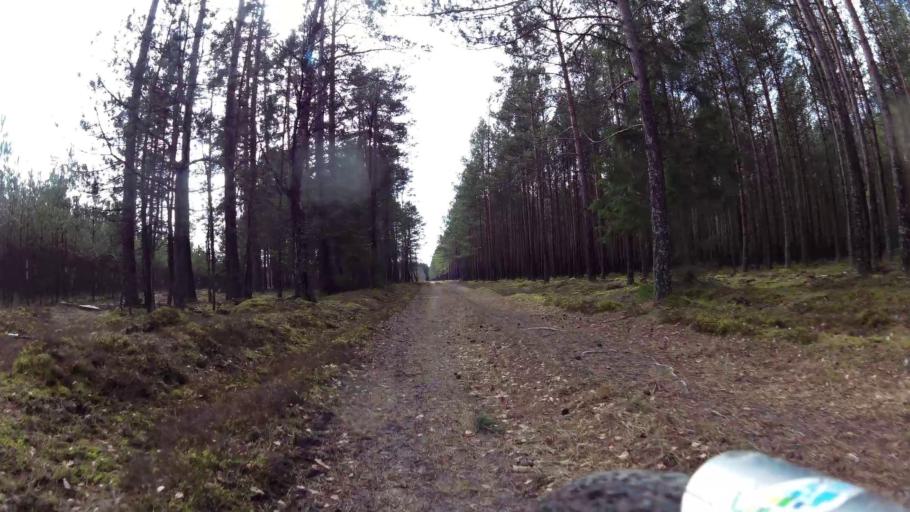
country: PL
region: Pomeranian Voivodeship
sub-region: Powiat bytowski
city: Kolczyglowy
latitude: 54.1914
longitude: 17.2147
